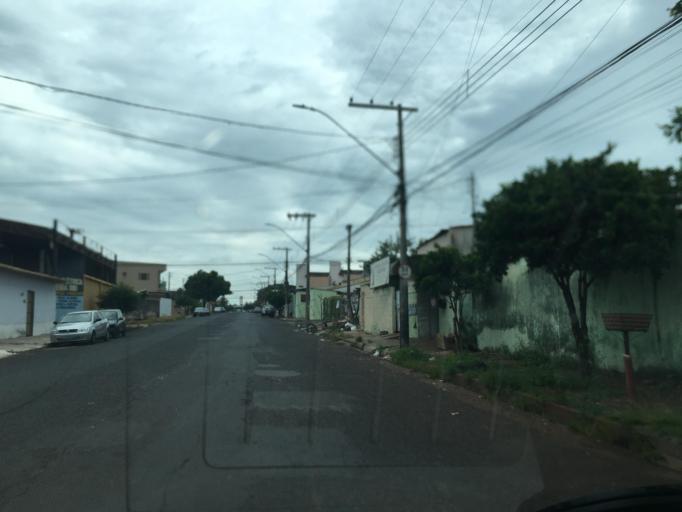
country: BR
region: Minas Gerais
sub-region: Uberlandia
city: Uberlandia
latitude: -18.9134
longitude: -48.3050
